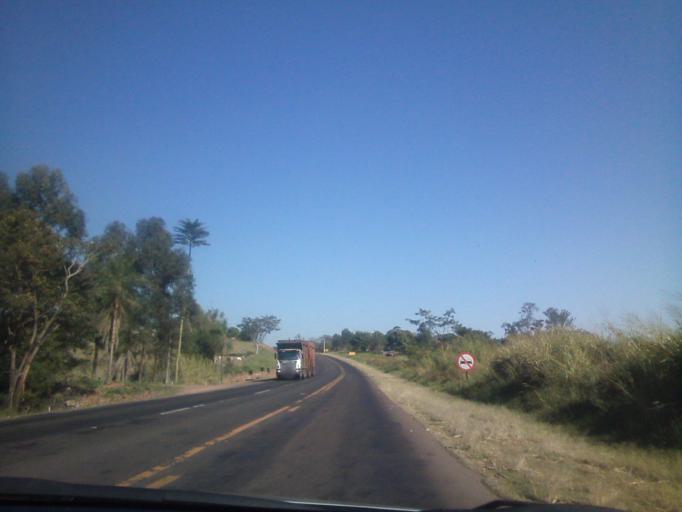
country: BR
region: Sao Paulo
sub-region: Pirapozinho
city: Pirapozinho
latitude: -22.2665
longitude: -51.5007
